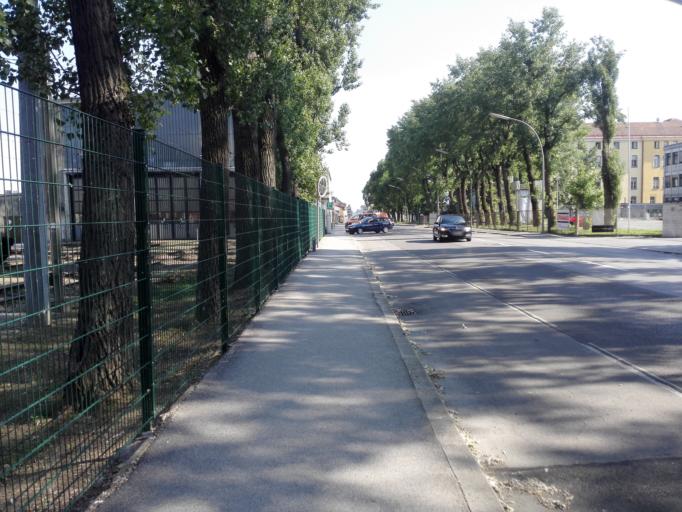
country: AT
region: Styria
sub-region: Graz Stadt
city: Wetzelsdorf
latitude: 47.0748
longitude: 15.4134
